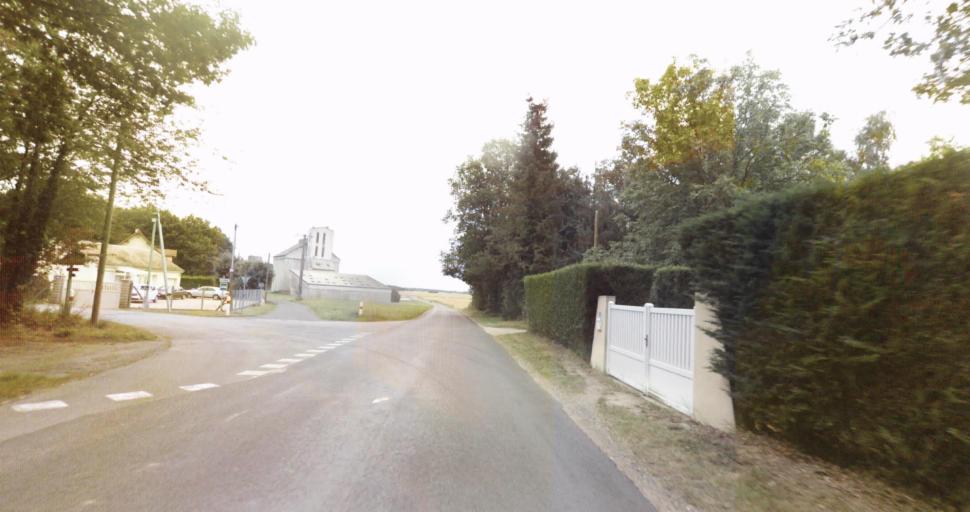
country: FR
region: Haute-Normandie
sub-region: Departement de l'Eure
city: Saint-Germain-sur-Avre
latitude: 48.8005
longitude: 1.2753
